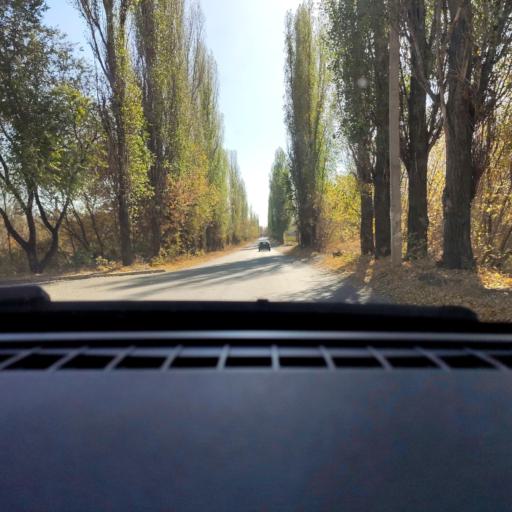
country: RU
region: Voronezj
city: Novaya Usman'
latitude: 51.6440
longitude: 39.3052
